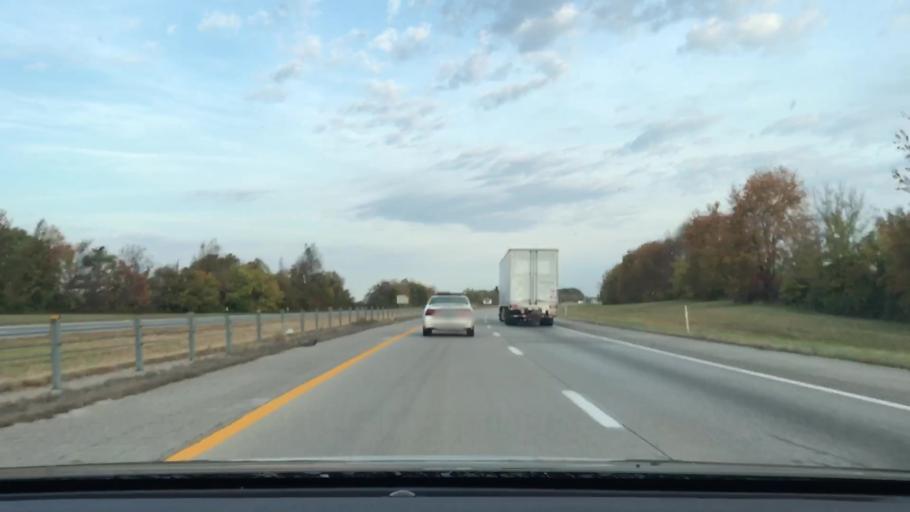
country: US
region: Kentucky
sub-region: Christian County
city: Oak Grove
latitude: 36.7156
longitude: -87.4819
